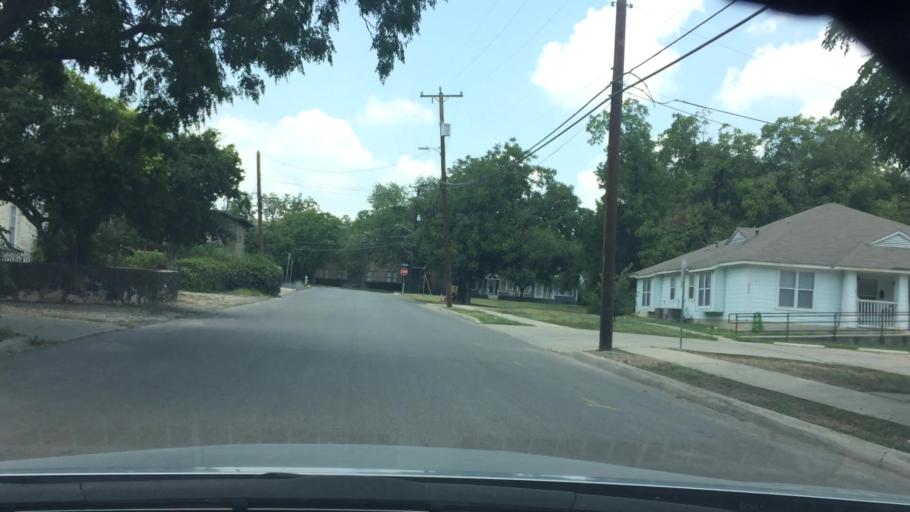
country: US
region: Texas
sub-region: Bexar County
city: Olmos Park
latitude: 29.4547
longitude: -98.4849
